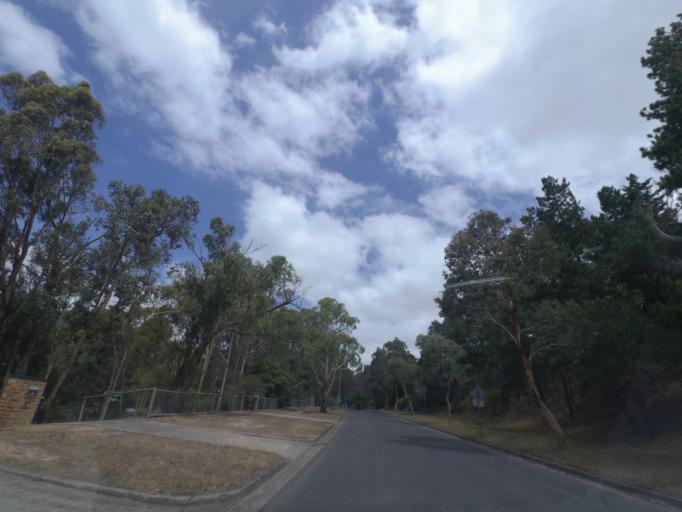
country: AU
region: Victoria
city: Mitcham
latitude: -37.8005
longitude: 145.2126
